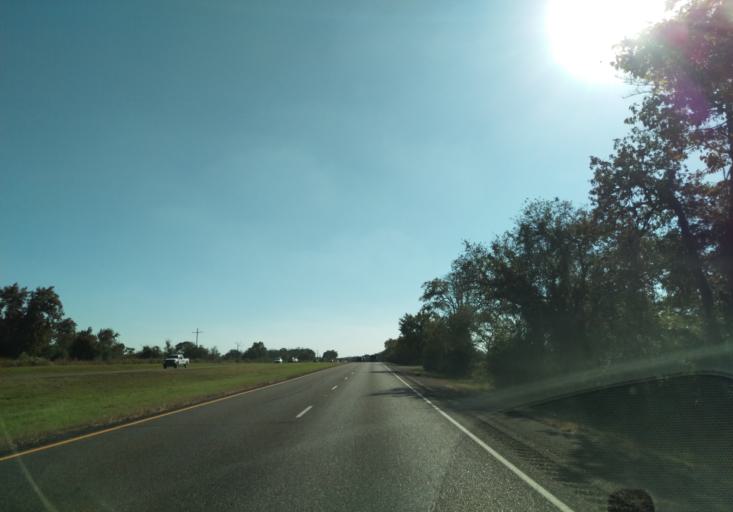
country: US
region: Texas
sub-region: Waller County
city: Hempstead
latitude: 30.2382
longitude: -96.0515
